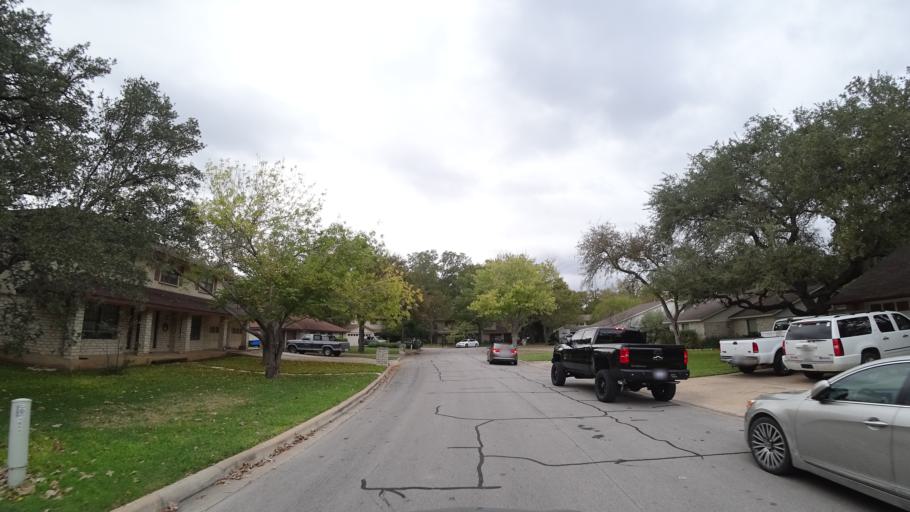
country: US
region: Texas
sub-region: Williamson County
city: Round Rock
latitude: 30.5011
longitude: -97.7006
